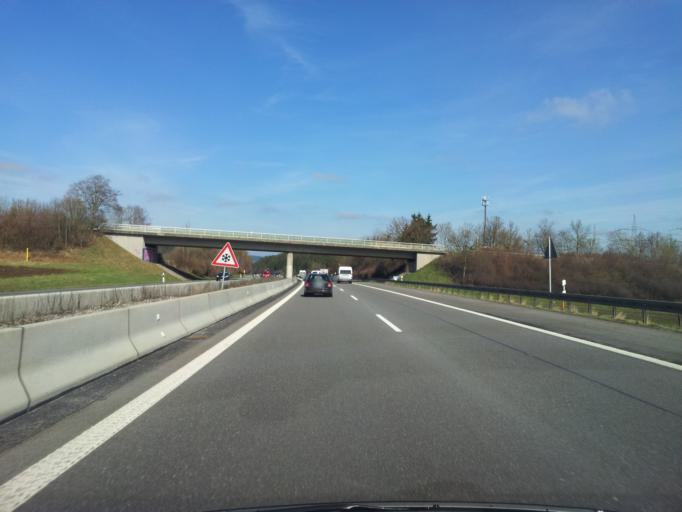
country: DE
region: Baden-Wuerttemberg
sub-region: Freiburg Region
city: Trossingen
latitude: 48.0602
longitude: 8.6185
